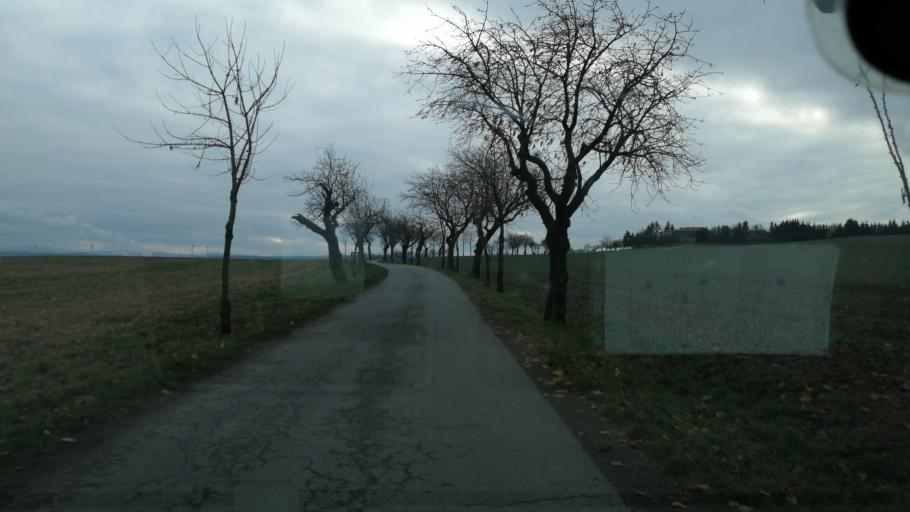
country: DE
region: Saxony
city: Bernstadt
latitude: 51.0598
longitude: 14.7988
